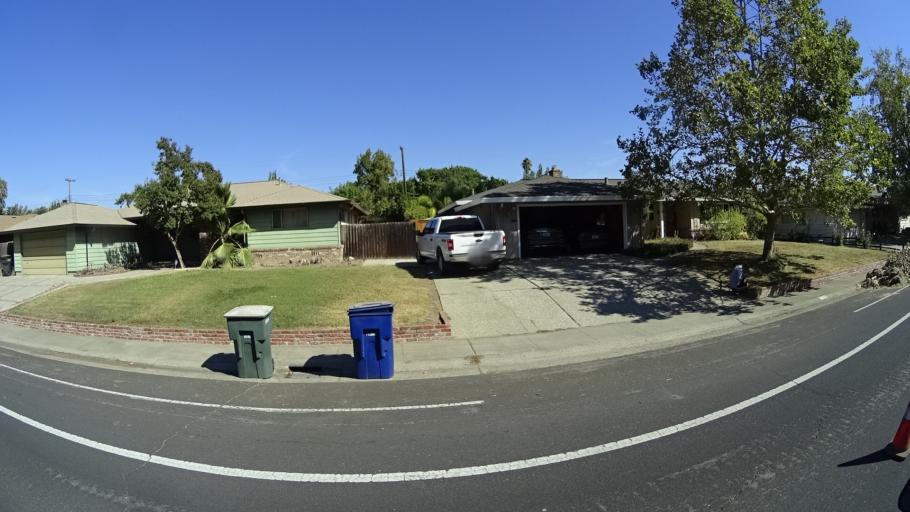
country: US
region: California
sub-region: Sacramento County
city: Parkway
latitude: 38.5053
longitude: -121.5096
